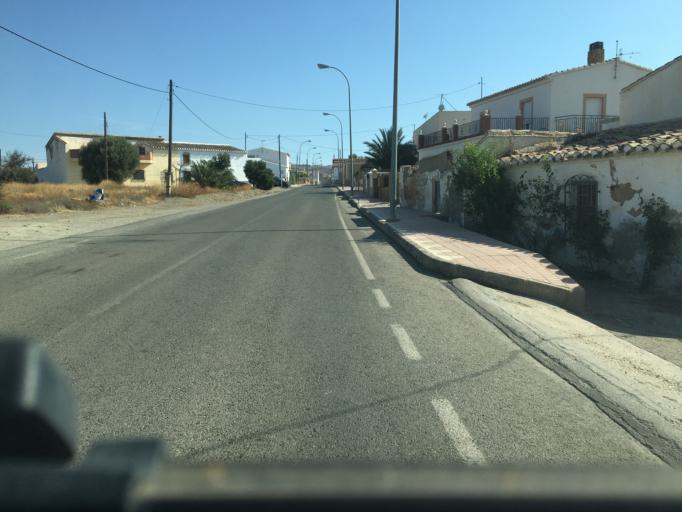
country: ES
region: Andalusia
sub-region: Provincia de Almeria
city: Huercal-Overa
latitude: 37.4651
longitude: -1.9874
